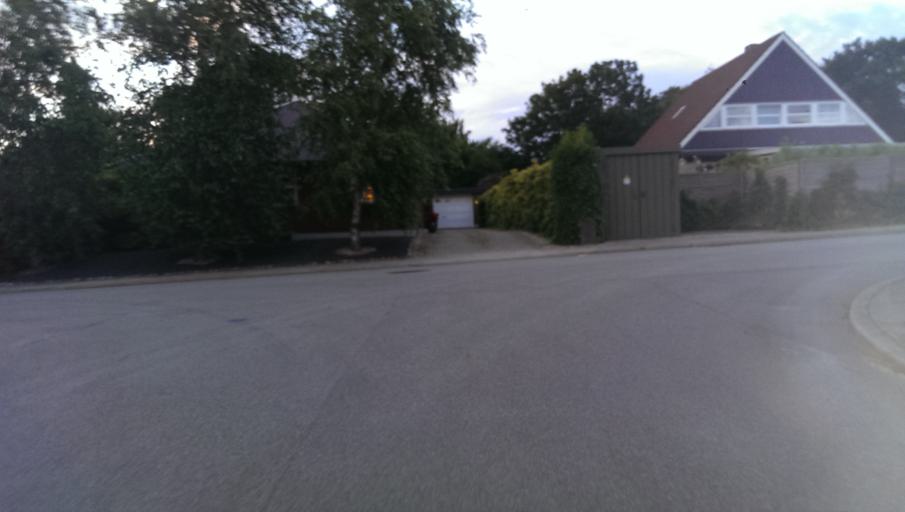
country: DK
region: South Denmark
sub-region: Esbjerg Kommune
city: Tjaereborg
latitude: 55.4718
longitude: 8.5725
